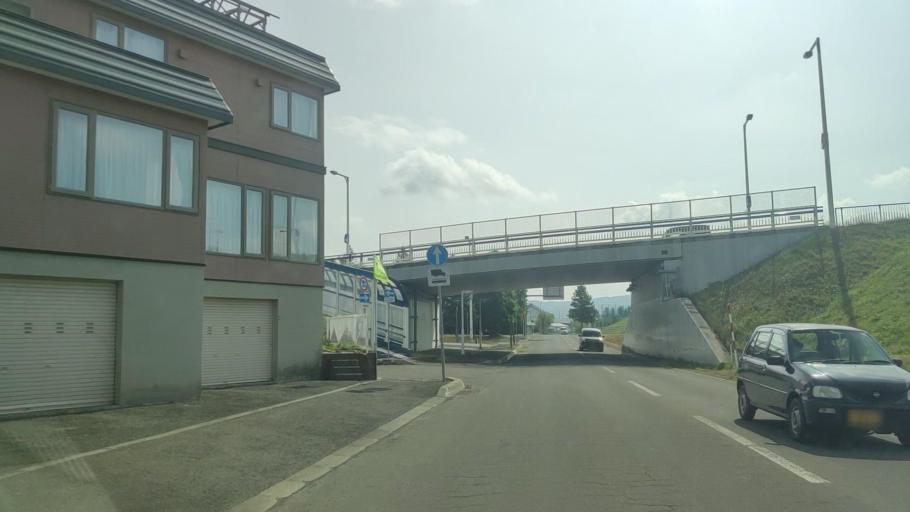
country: JP
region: Hokkaido
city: Shimo-furano
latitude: 43.3394
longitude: 142.3848
